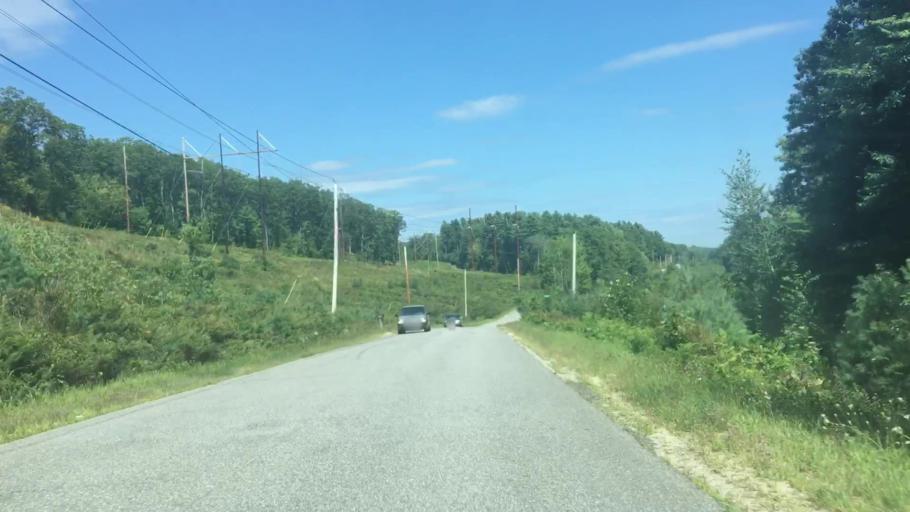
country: US
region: Maine
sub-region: Kennebec County
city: Monmouth
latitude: 44.1982
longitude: -69.9633
